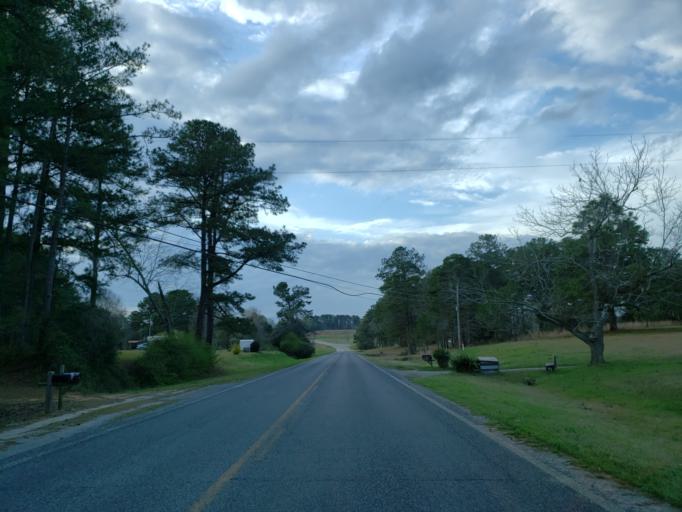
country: US
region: Mississippi
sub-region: Clarke County
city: Stonewall
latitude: 32.2087
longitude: -88.6933
